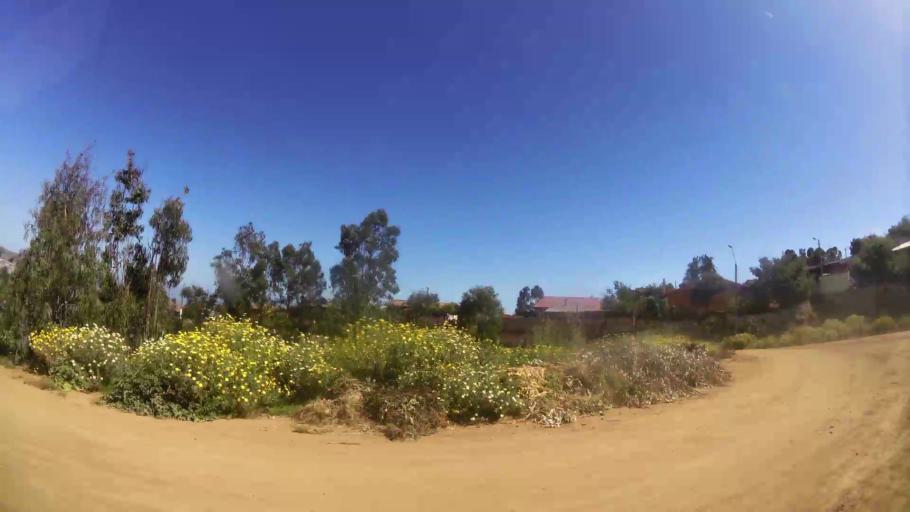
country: CL
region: Valparaiso
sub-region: Provincia de Valparaiso
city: Vina del Mar
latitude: -33.0643
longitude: -71.5782
